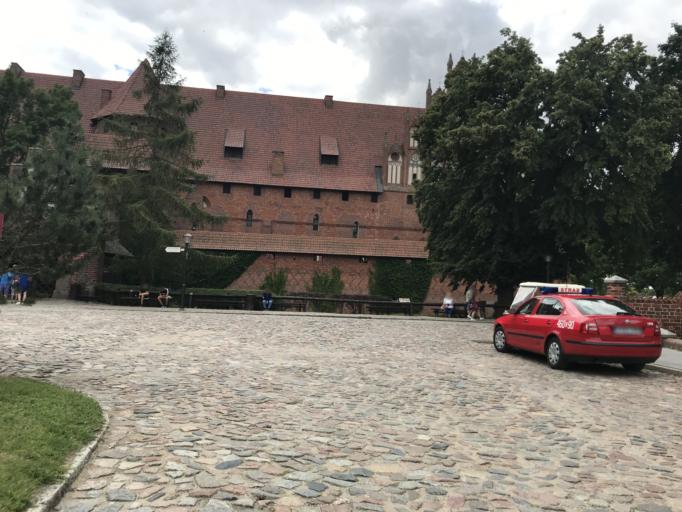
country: PL
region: Pomeranian Voivodeship
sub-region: Powiat malborski
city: Malbork
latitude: 54.0412
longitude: 19.0298
